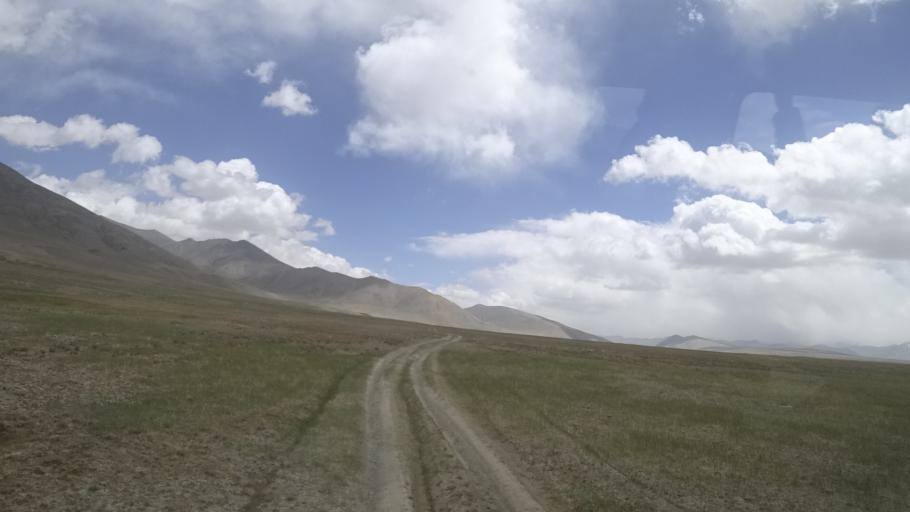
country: TJ
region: Gorno-Badakhshan
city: Murghob
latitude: 37.4847
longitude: 73.9862
